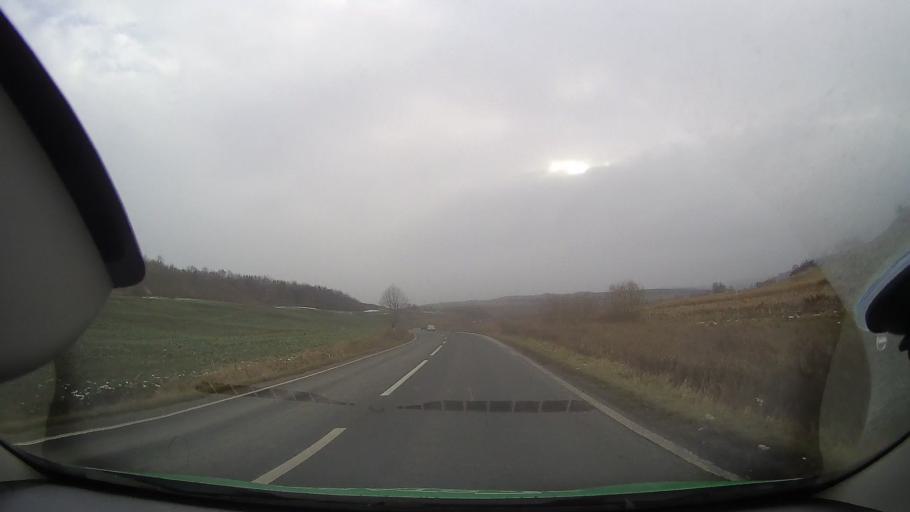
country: RO
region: Sibiu
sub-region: Comuna Blajel
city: Blajel
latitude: 46.2258
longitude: 24.3132
